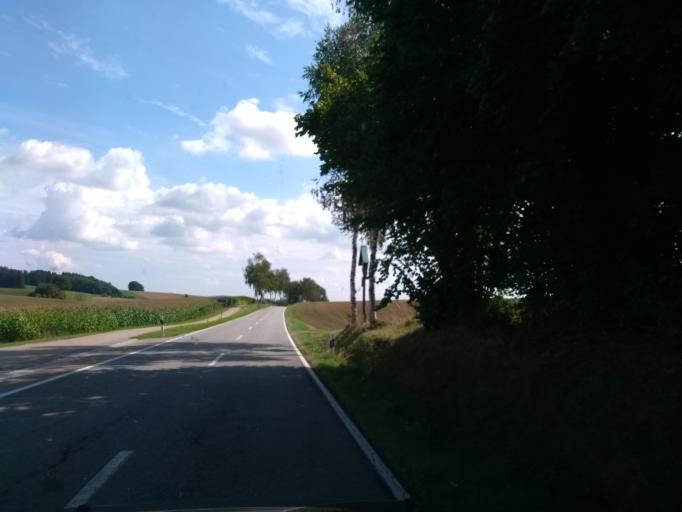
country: DE
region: Bavaria
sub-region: Upper Bavaria
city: Schwabhausen
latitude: 48.3941
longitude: 11.3486
